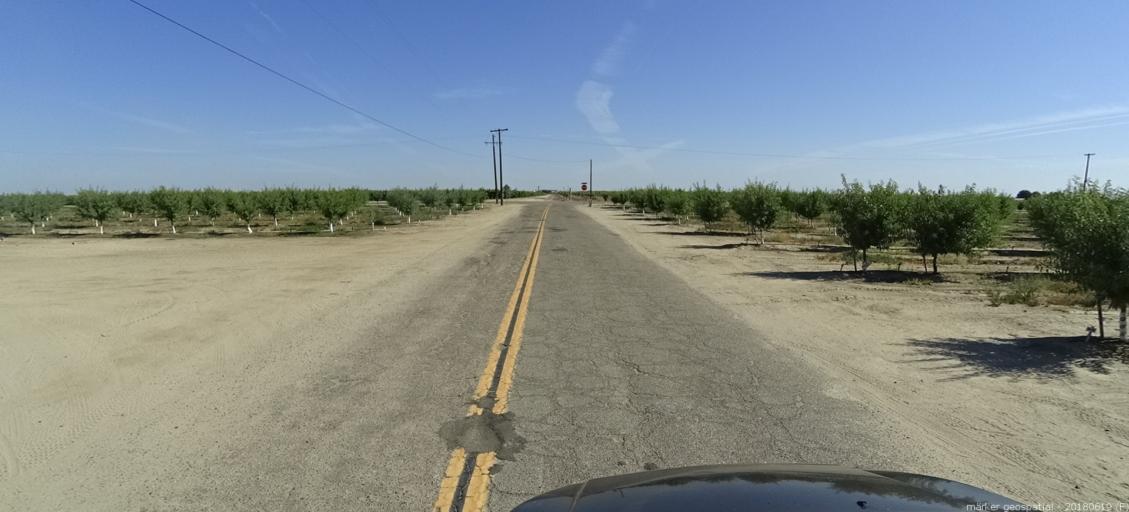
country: US
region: California
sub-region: Fresno County
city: Biola
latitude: 36.8287
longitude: -120.0653
